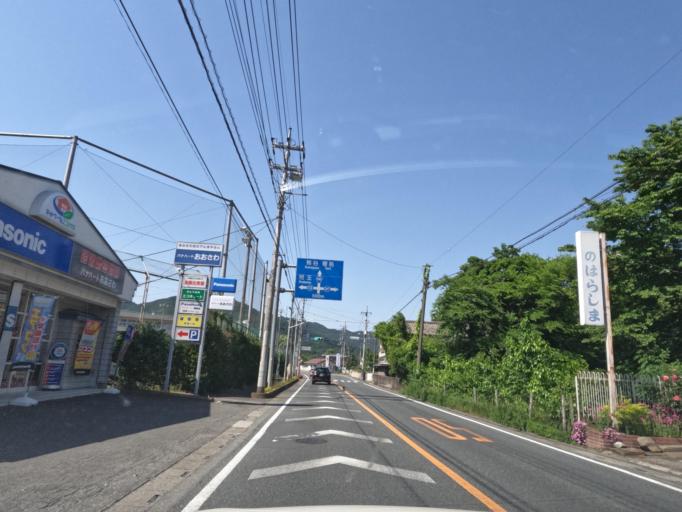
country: JP
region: Saitama
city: Kodamacho-kodamaminami
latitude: 36.1133
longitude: 139.1100
